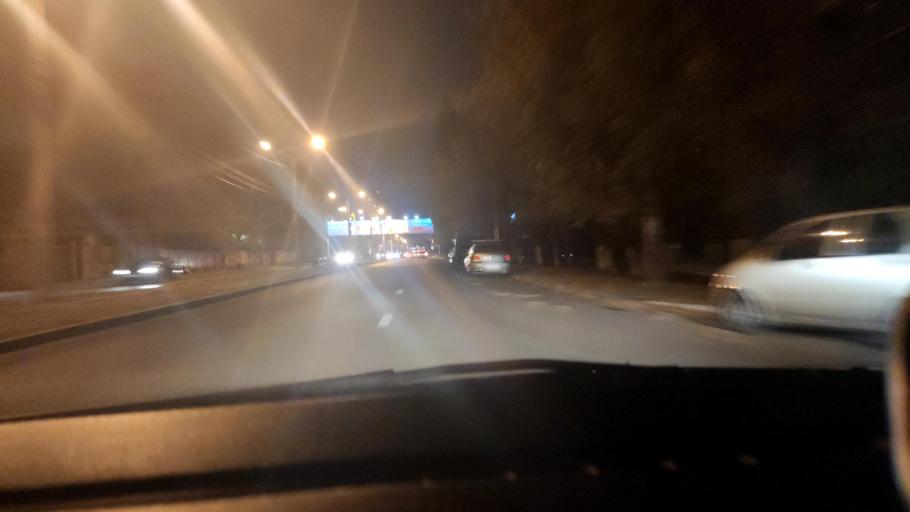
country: RU
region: Voronezj
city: Voronezh
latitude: 51.7059
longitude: 39.1955
